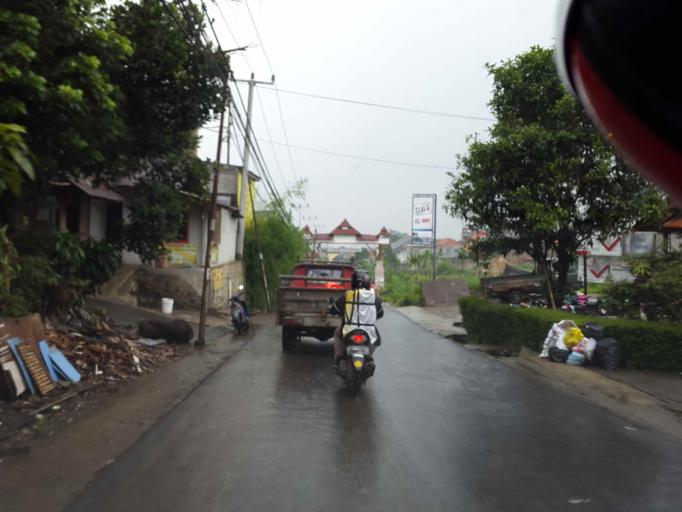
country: ID
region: West Java
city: Cimahi
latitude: -6.8564
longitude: 107.5789
